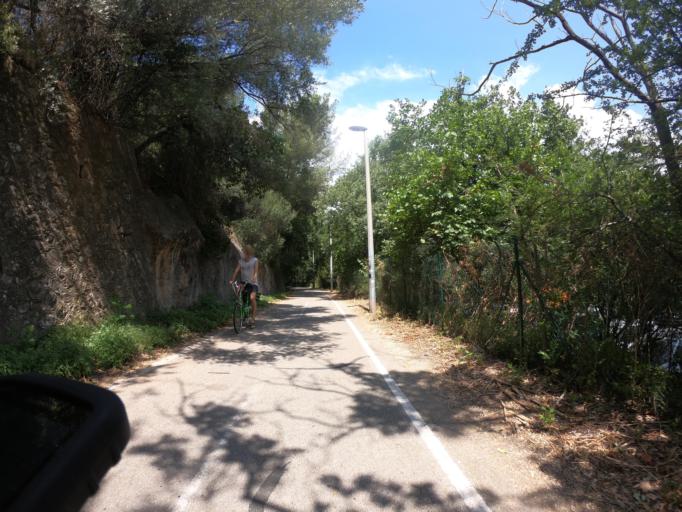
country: FR
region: Provence-Alpes-Cote d'Azur
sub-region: Departement du Var
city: La Valette-du-Var
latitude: 43.1226
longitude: 5.9629
